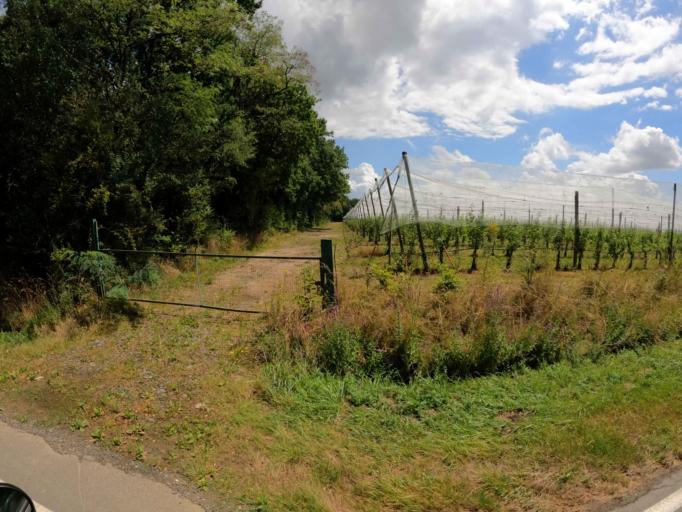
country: FR
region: Pays de la Loire
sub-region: Departement de Maine-et-Loire
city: Champigne
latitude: 47.6864
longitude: -0.5543
